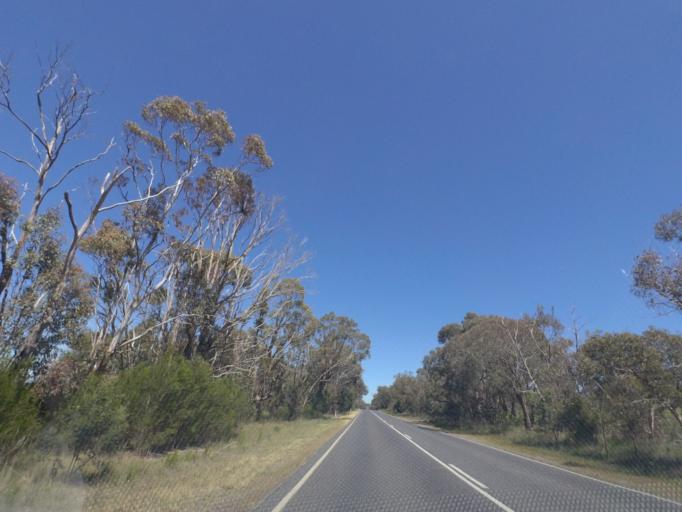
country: AU
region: Victoria
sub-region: Hume
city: Craigieburn
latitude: -37.2973
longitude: 144.8745
